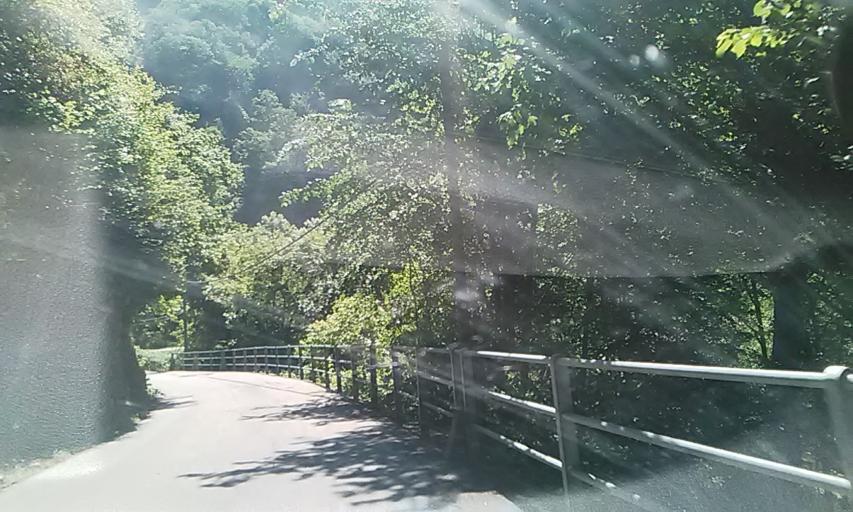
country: IT
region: Piedmont
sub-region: Provincia di Vercelli
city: Varallo
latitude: 45.8253
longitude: 8.2767
